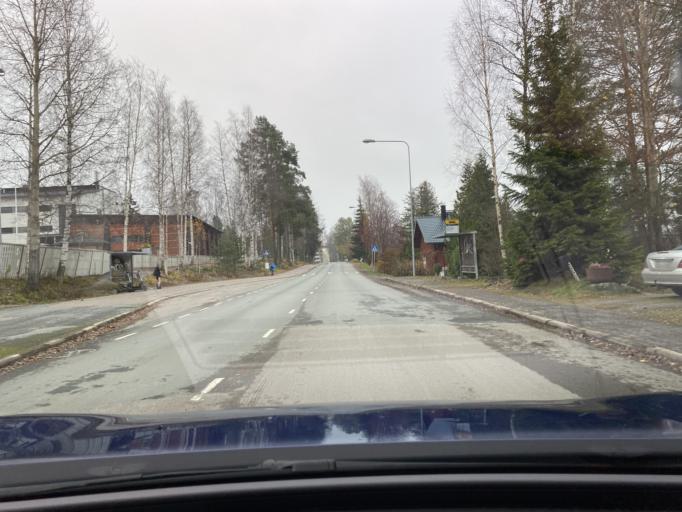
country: FI
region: Pirkanmaa
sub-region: Tampere
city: Nokia
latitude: 61.4597
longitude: 23.4924
